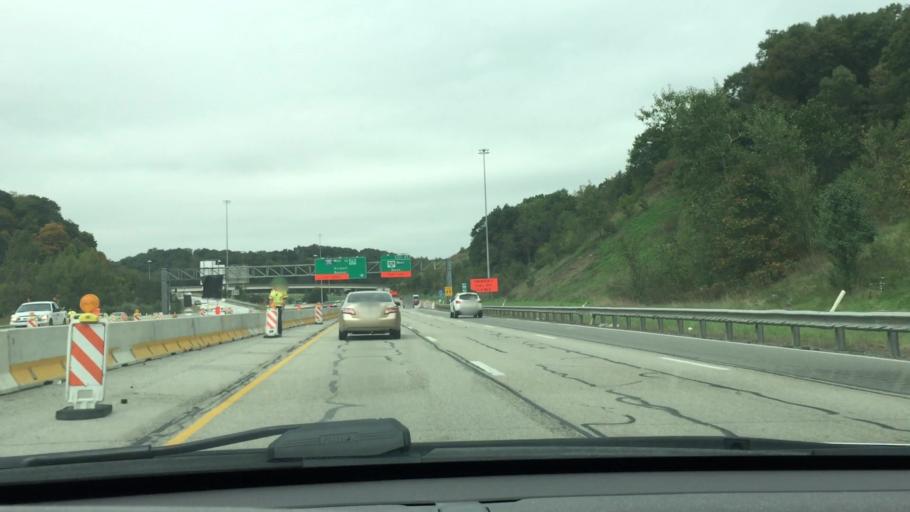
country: US
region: Pennsylvania
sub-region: Allegheny County
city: Enlow
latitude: 40.4637
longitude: -80.1941
